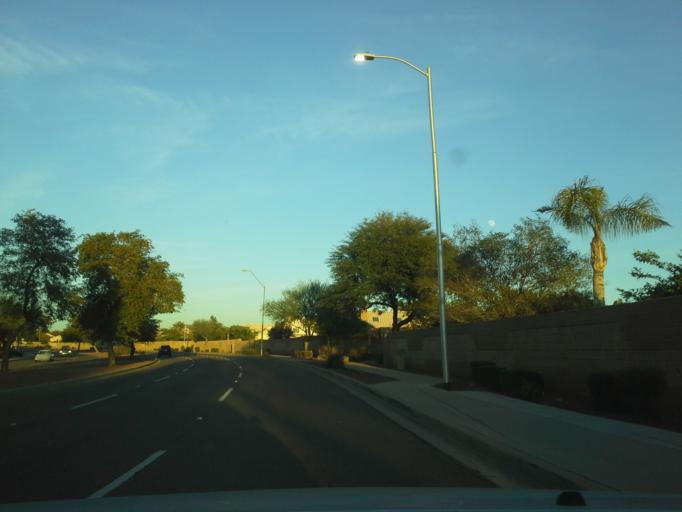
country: US
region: Arizona
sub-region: Maricopa County
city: Glendale
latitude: 33.6267
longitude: -112.0900
